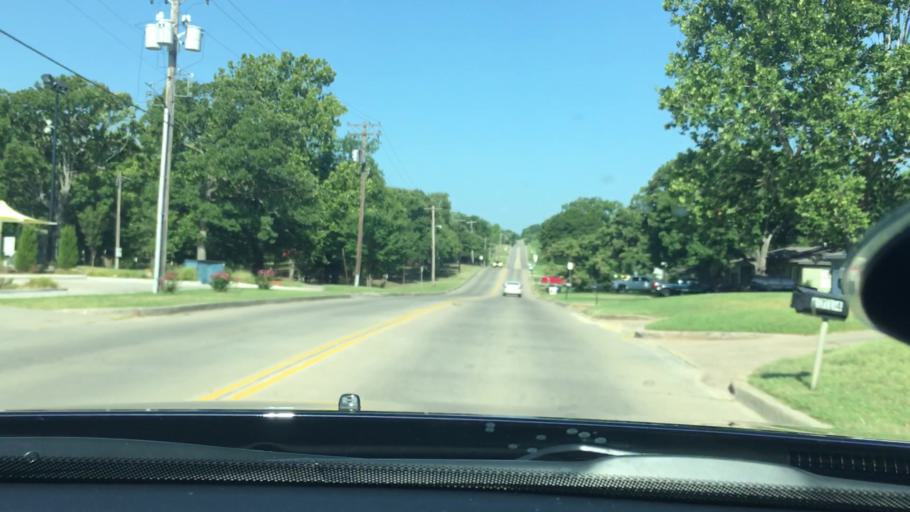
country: US
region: Oklahoma
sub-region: Pontotoc County
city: Ada
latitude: 34.7671
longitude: -96.6537
